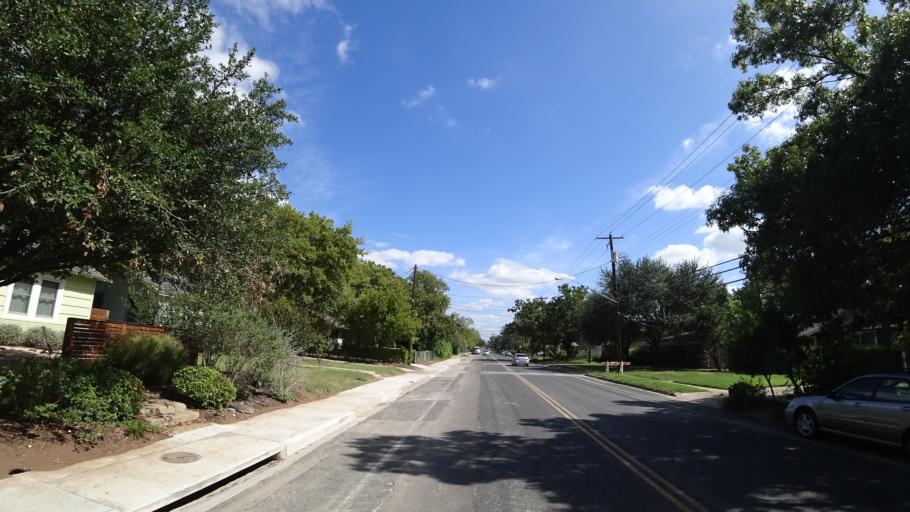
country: US
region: Texas
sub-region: Travis County
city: Austin
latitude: 30.3431
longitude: -97.7317
